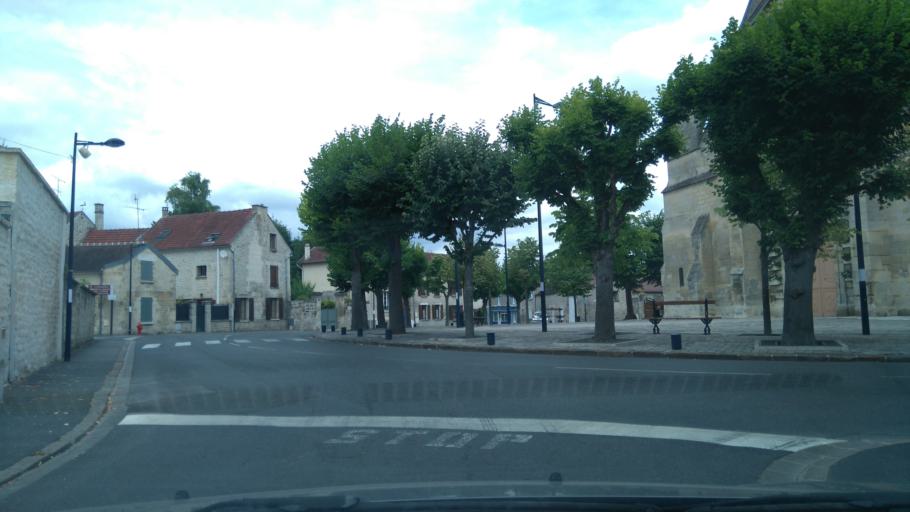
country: FR
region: Picardie
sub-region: Departement de l'Oise
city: Gouvieux
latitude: 49.1894
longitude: 2.4152
